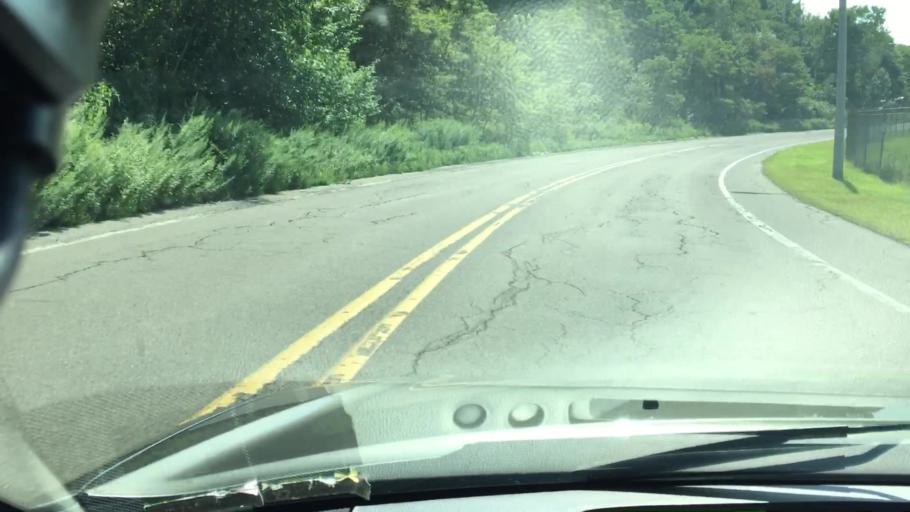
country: US
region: Pennsylvania
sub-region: Luzerne County
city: Plymouth
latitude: 41.1956
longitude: -75.9429
